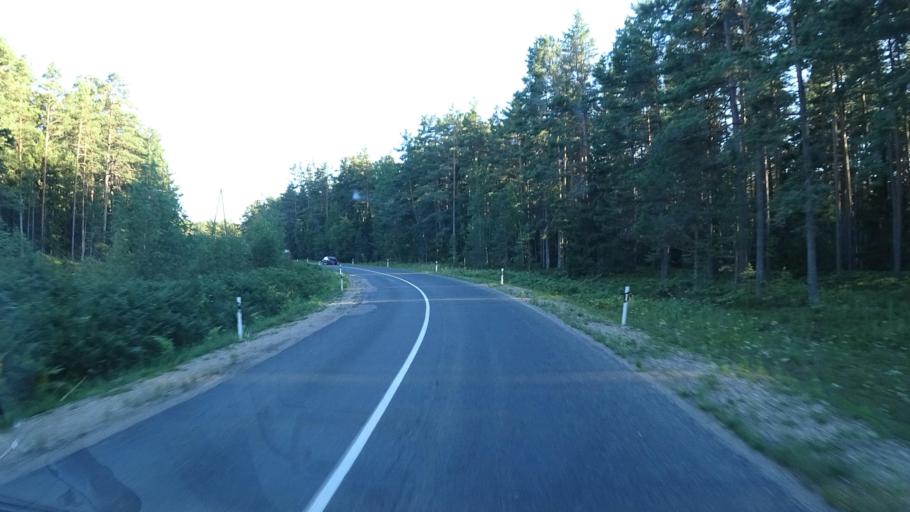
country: LV
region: Dundaga
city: Dundaga
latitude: 57.6852
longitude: 22.5693
